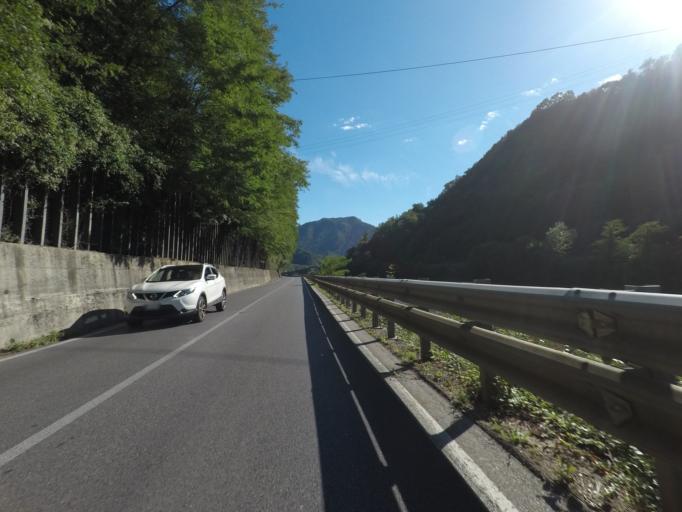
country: IT
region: Tuscany
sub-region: Provincia di Lucca
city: Bagni di Lucca
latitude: 43.9912
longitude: 10.5531
